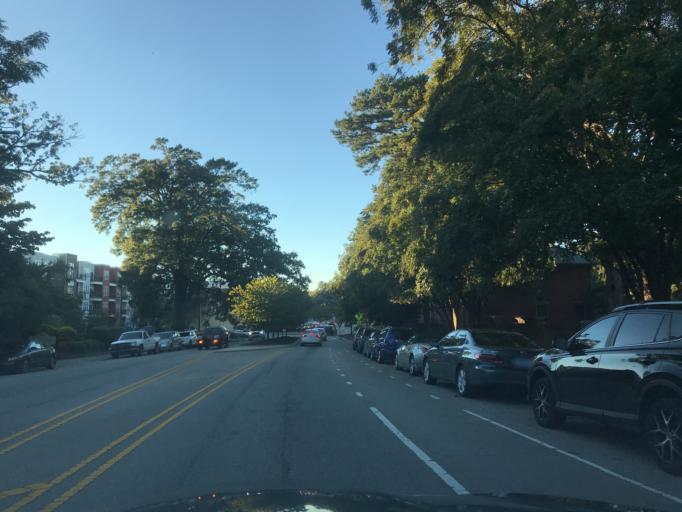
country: US
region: North Carolina
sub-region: Wake County
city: West Raleigh
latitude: 35.7821
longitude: -78.6543
